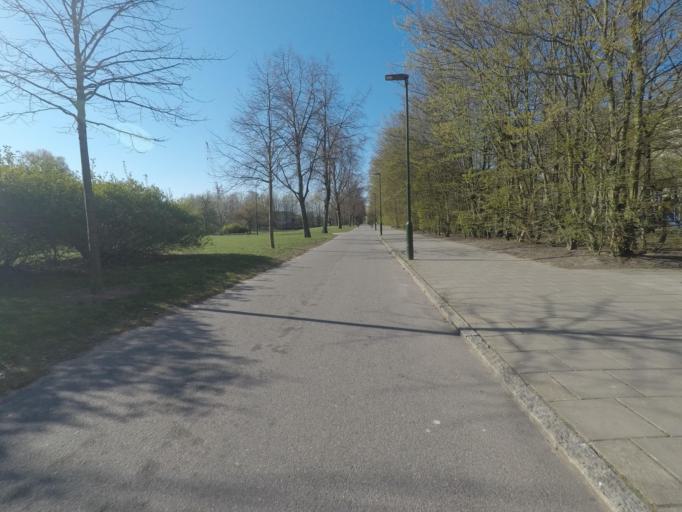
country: SE
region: Skane
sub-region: Malmo
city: Malmoe
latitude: 55.5626
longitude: 13.0134
